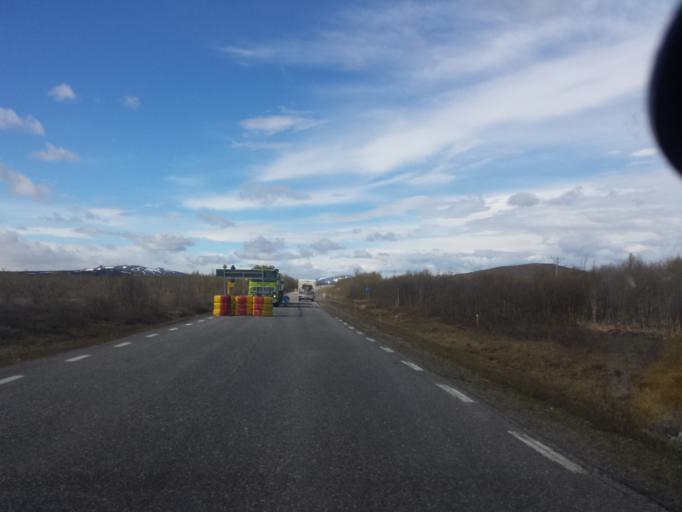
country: SE
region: Norrbotten
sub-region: Kiruna Kommun
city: Kiruna
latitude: 68.0139
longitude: 19.8413
